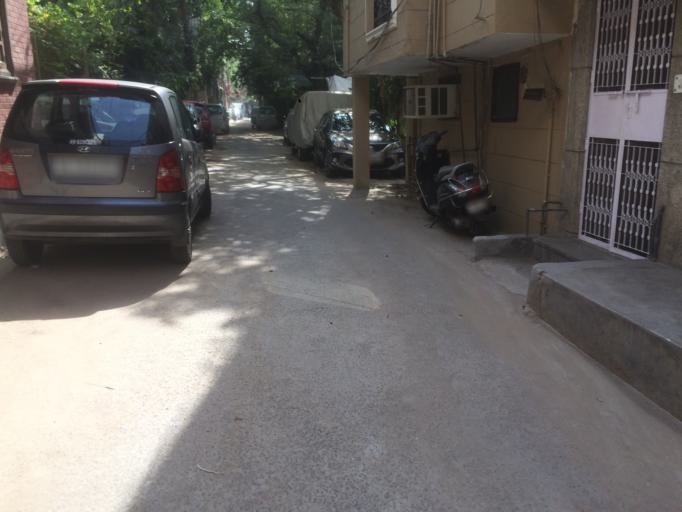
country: IN
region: NCT
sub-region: New Delhi
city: New Delhi
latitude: 28.5613
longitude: 77.2464
